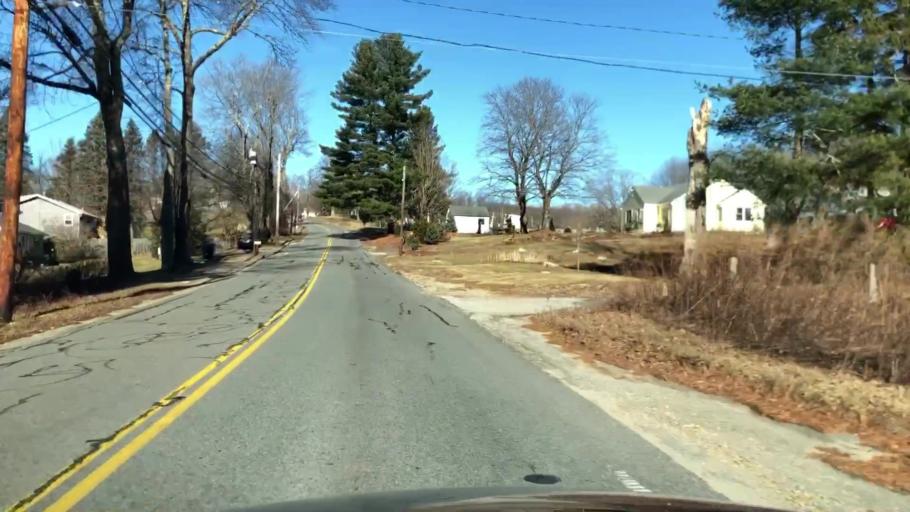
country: US
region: Massachusetts
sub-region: Worcester County
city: Charlton
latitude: 42.1289
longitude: -71.9692
